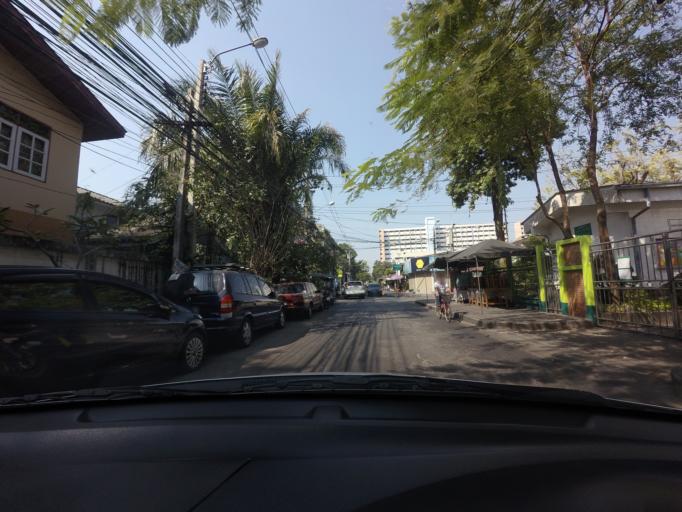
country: TH
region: Bangkok
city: Khlong Toei
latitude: 13.7277
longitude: 100.5503
